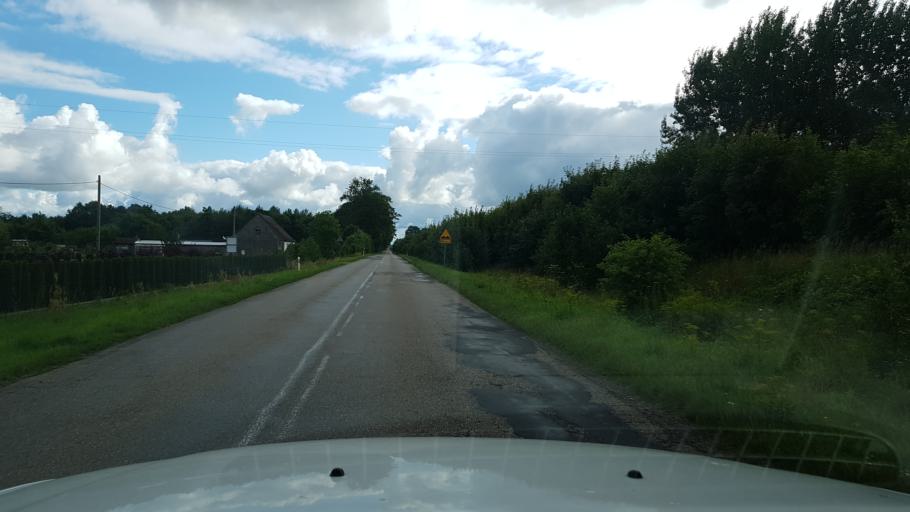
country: PL
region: West Pomeranian Voivodeship
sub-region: Powiat swidwinski
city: Rabino
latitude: 53.7764
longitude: 15.9789
